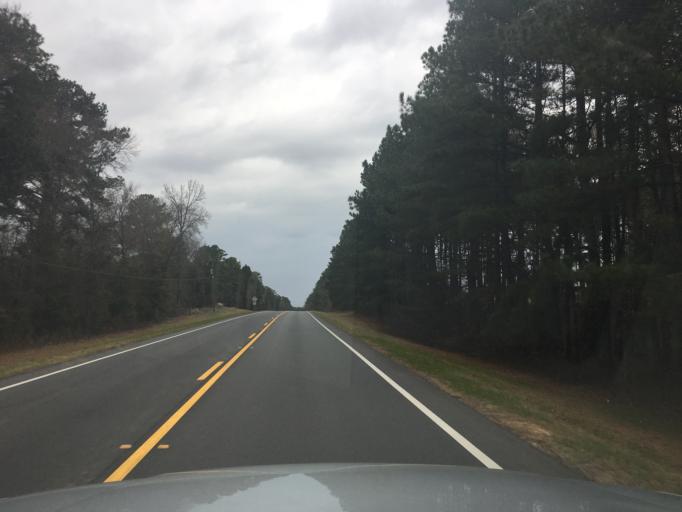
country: US
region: Georgia
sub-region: Columbia County
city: Appling
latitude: 33.6753
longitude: -82.3363
